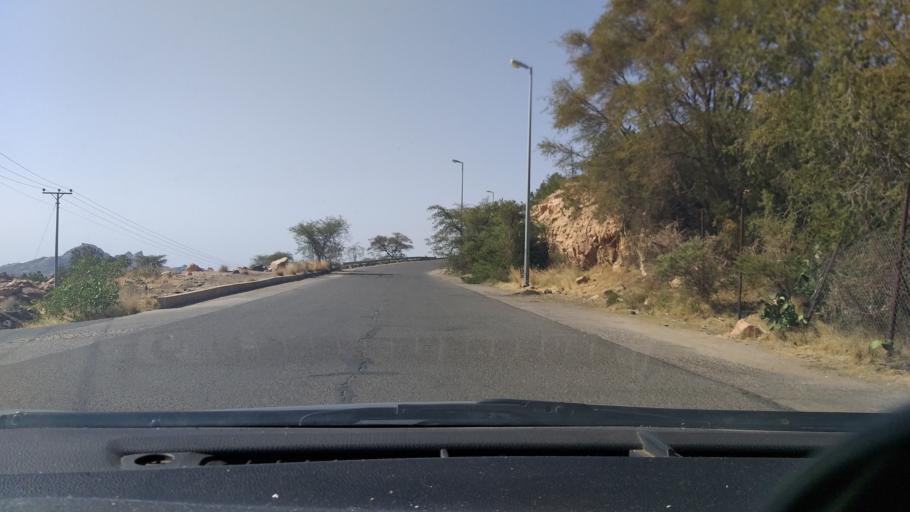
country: SA
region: Makkah
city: Ash Shafa
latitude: 21.0615
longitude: 40.3239
